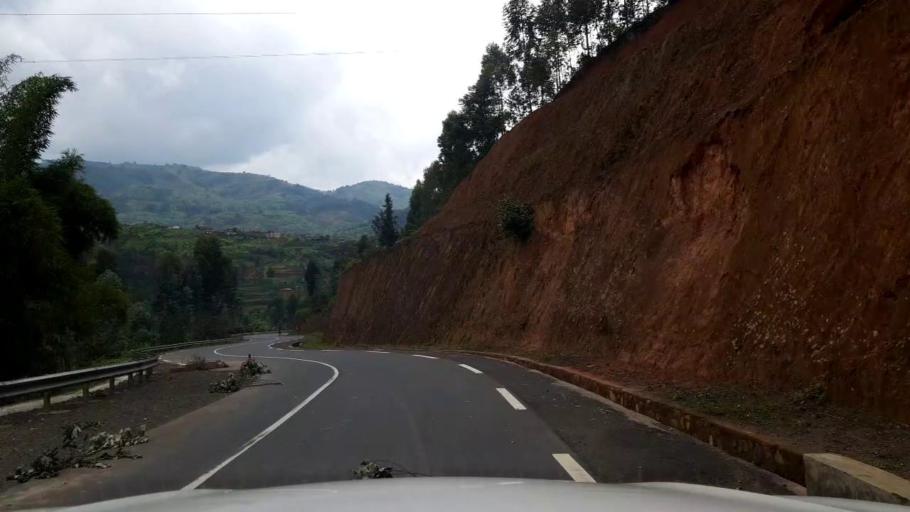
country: RW
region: Western Province
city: Kibuye
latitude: -1.9096
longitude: 29.3674
